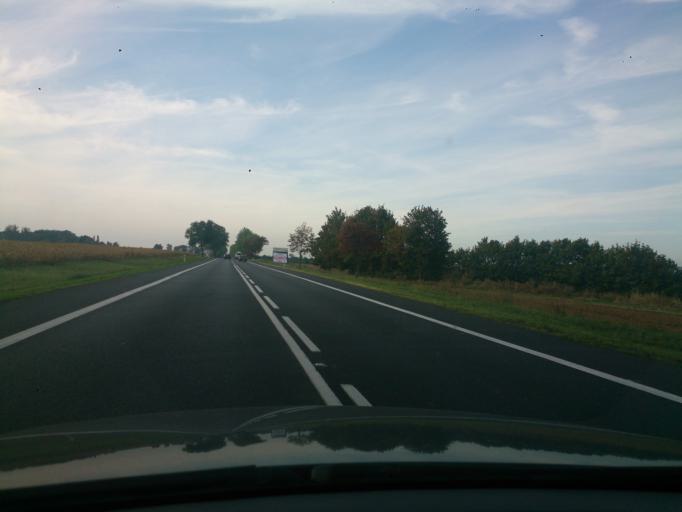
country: PL
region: Kujawsko-Pomorskie
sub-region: Powiat swiecki
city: Pruszcz
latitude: 53.3259
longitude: 18.2848
